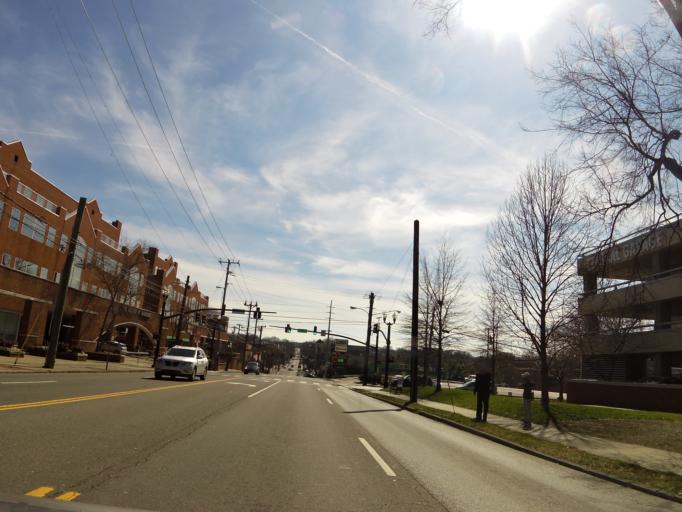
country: US
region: Tennessee
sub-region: Davidson County
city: Nashville
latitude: 36.1402
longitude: -86.8005
